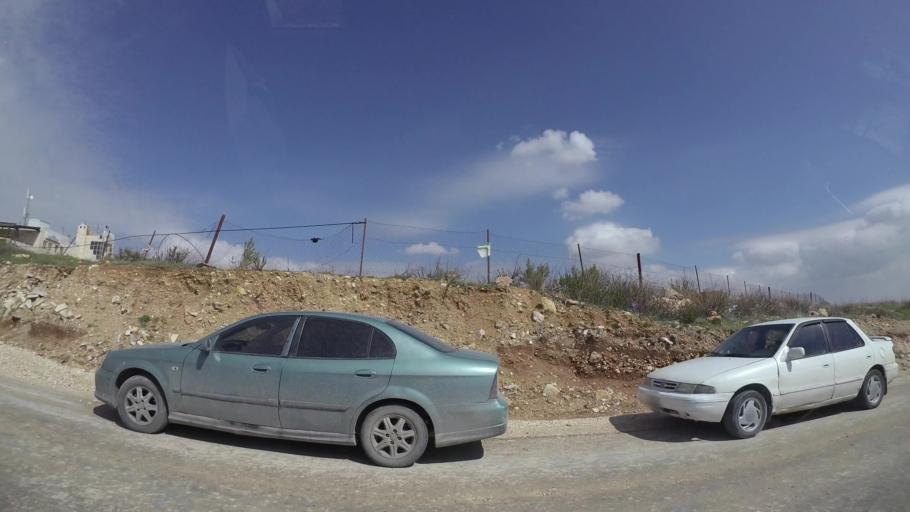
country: JO
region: Amman
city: Al Jubayhah
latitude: 31.9978
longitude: 35.9034
